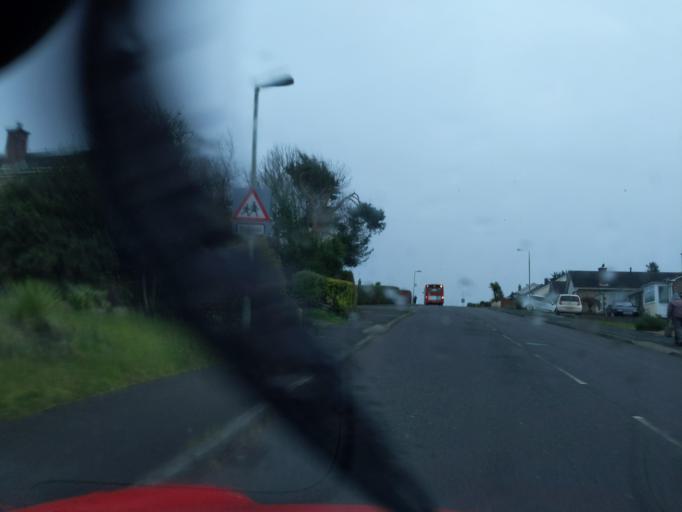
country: GB
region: England
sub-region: Devon
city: Wembury
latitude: 50.3268
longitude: -4.0712
